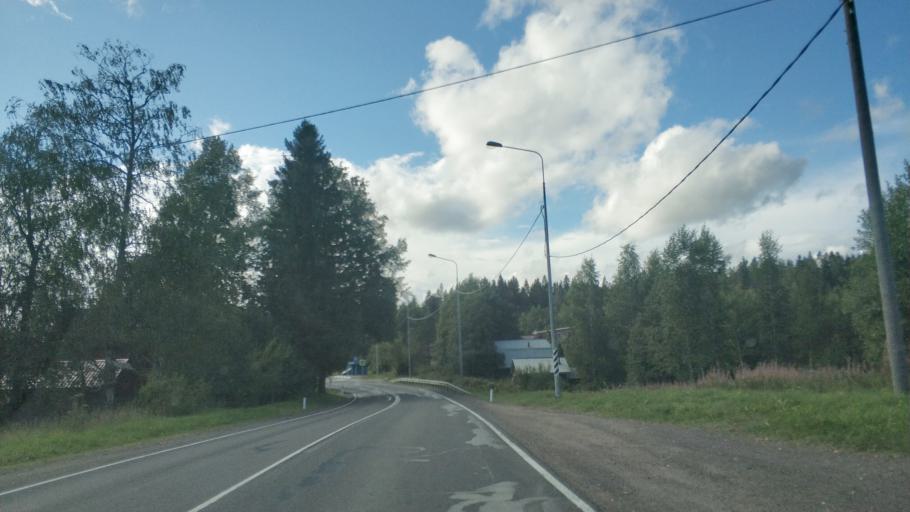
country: RU
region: Republic of Karelia
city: Lakhdenpokh'ya
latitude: 61.5106
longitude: 30.0837
